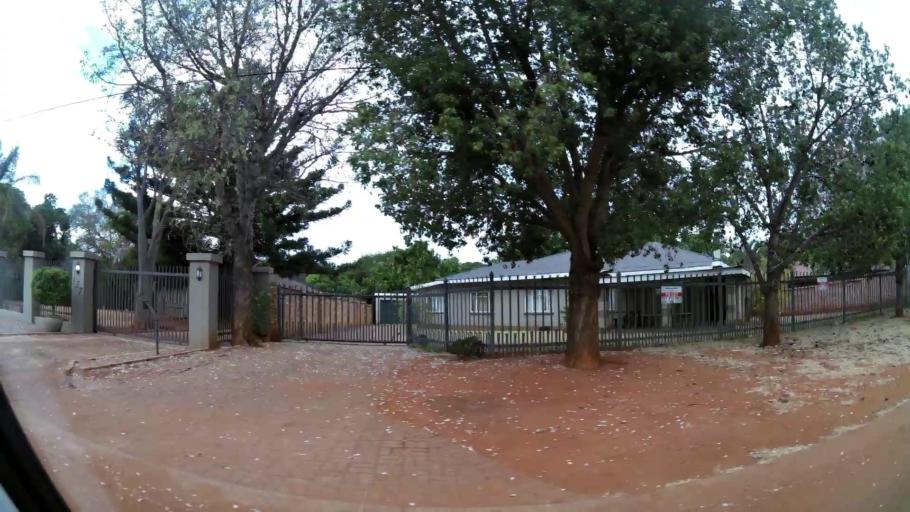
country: ZA
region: Limpopo
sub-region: Waterberg District Municipality
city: Modimolle
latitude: -24.5083
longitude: 28.7196
